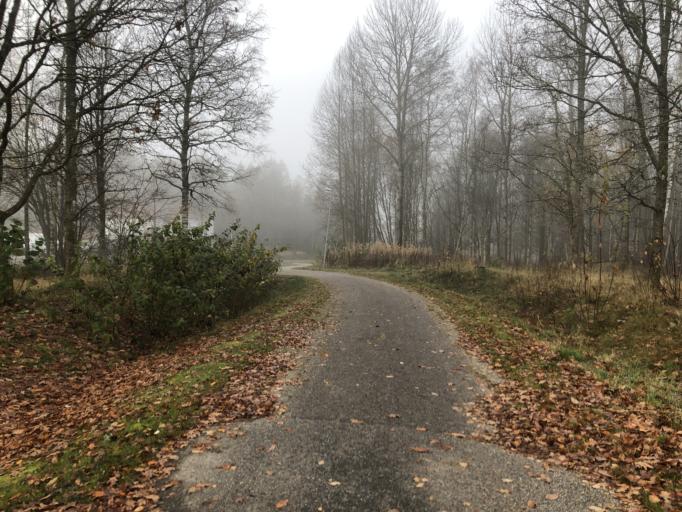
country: SE
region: Vaestra Goetaland
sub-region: Ulricehamns Kommun
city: Ulricehamn
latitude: 57.6765
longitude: 13.4604
